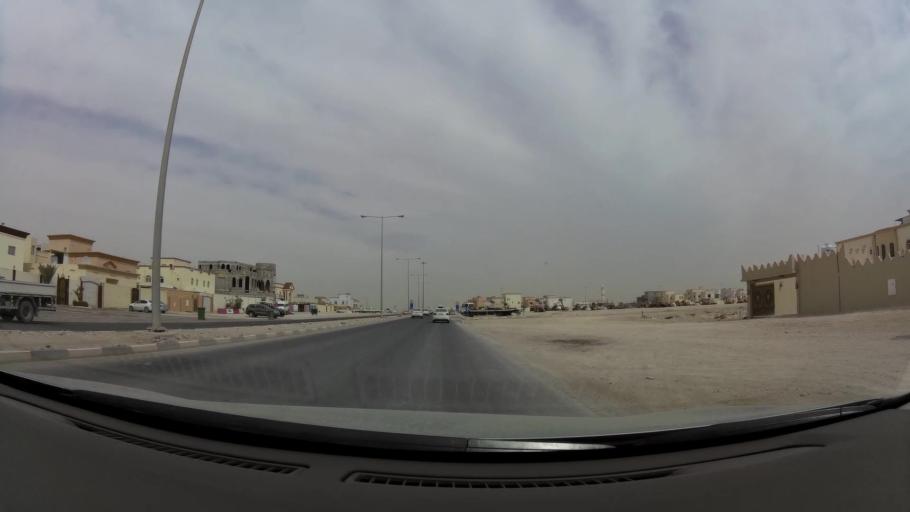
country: QA
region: Baladiyat ad Dawhah
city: Doha
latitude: 25.2110
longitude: 51.4830
